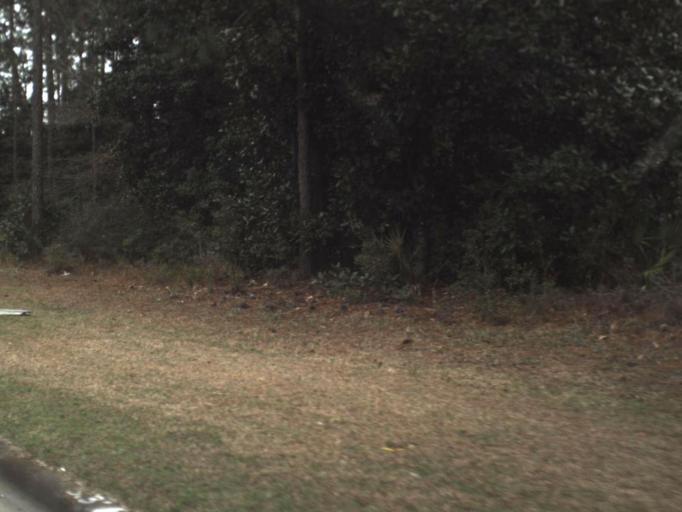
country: US
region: Florida
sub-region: Bay County
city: Springfield
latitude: 30.1703
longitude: -85.5913
